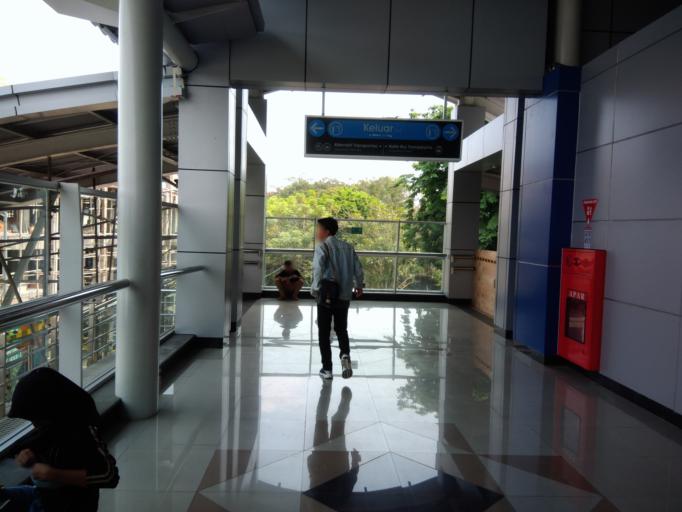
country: ID
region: West Java
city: Bekasi
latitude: -6.2191
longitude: 106.9523
